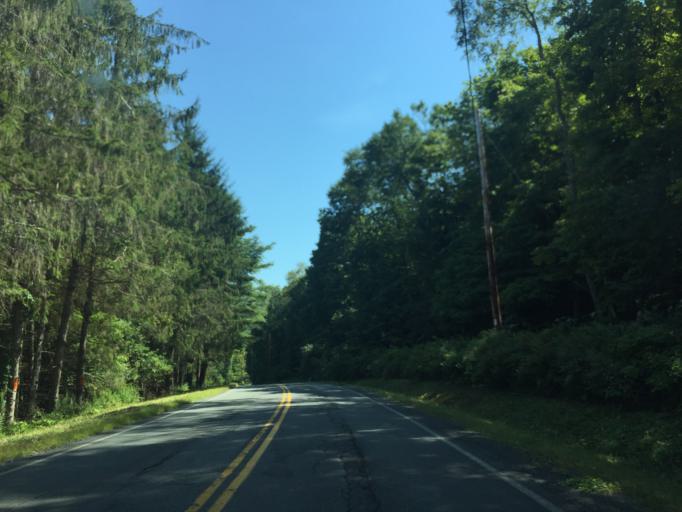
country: US
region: New York
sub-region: Sullivan County
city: Livingston Manor
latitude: 41.8871
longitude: -74.9198
